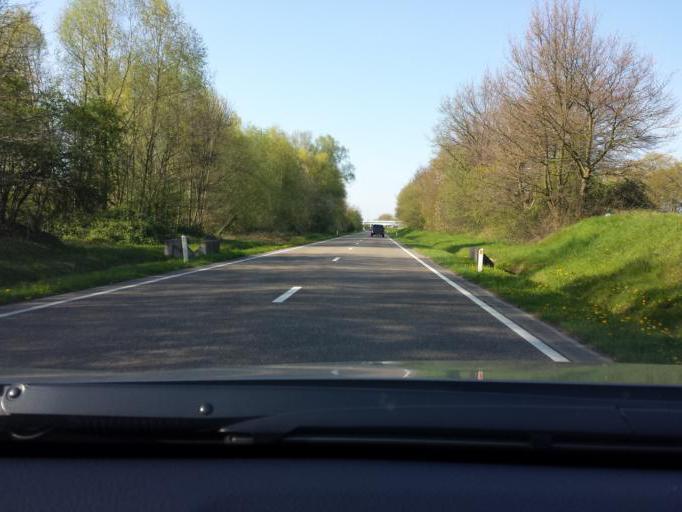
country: BE
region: Flanders
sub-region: Provincie Limburg
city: Maasmechelen
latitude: 50.9540
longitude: 5.7092
